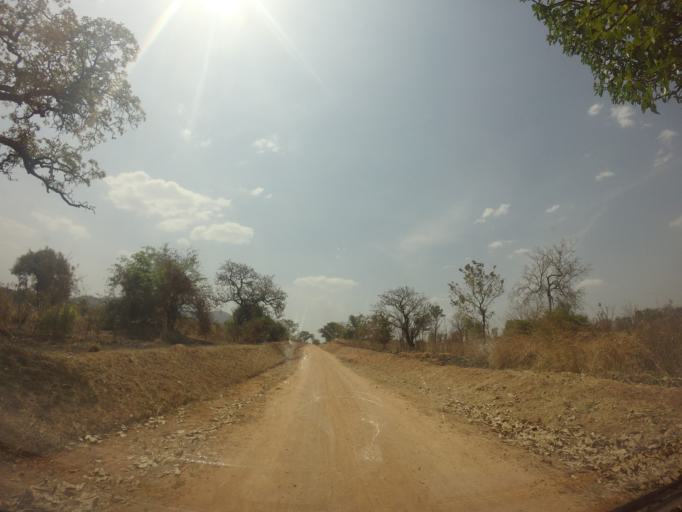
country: UG
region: Northern Region
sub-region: Arua District
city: Arua
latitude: 2.8968
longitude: 31.1166
